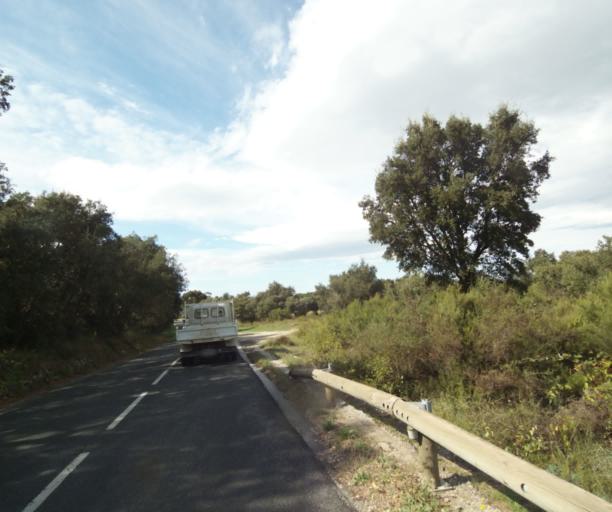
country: FR
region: Languedoc-Roussillon
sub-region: Departement des Pyrenees-Orientales
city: Sorede
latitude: 42.5310
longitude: 2.9705
